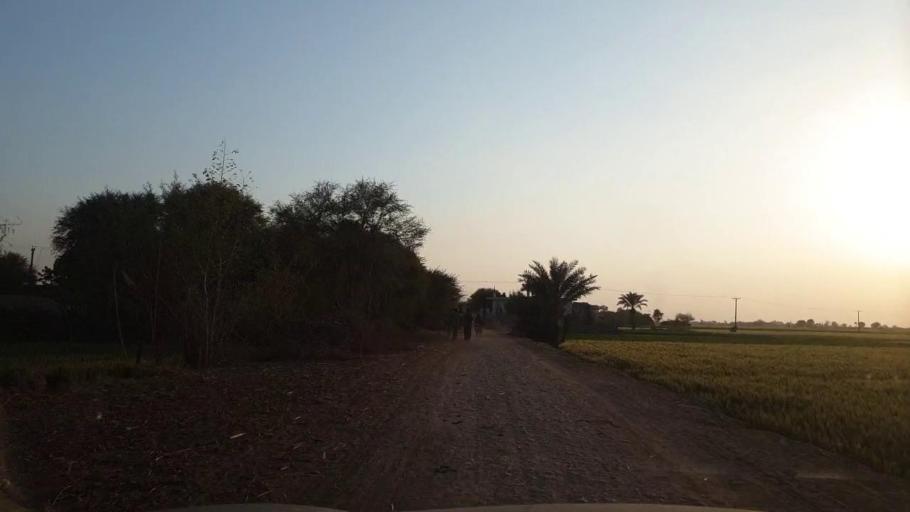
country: PK
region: Sindh
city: Berani
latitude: 25.6735
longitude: 68.7637
